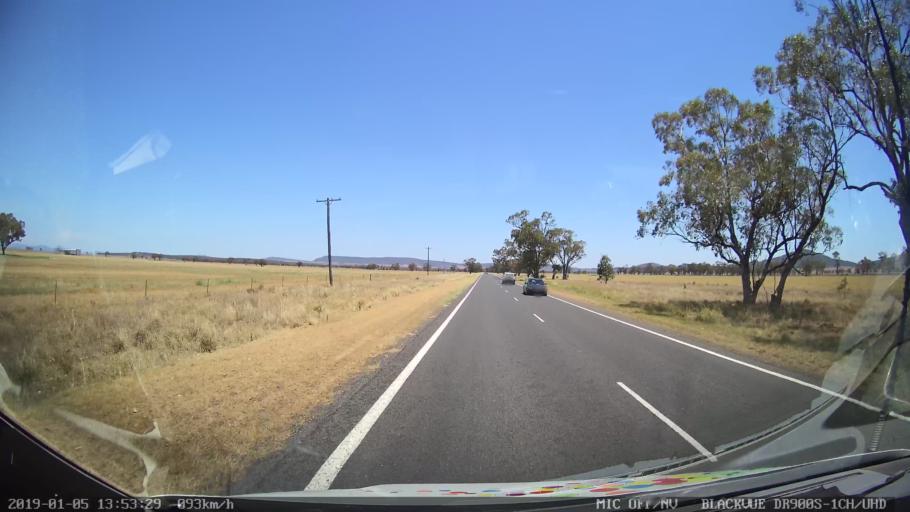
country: AU
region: New South Wales
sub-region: Gunnedah
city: Gunnedah
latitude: -31.0755
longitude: 150.2773
